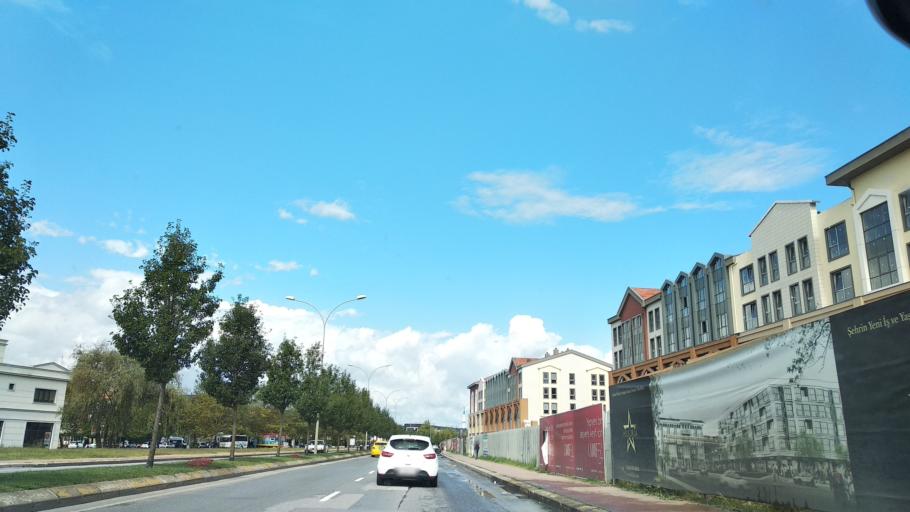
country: TR
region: Sakarya
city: Adapazari
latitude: 40.7737
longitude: 30.3642
